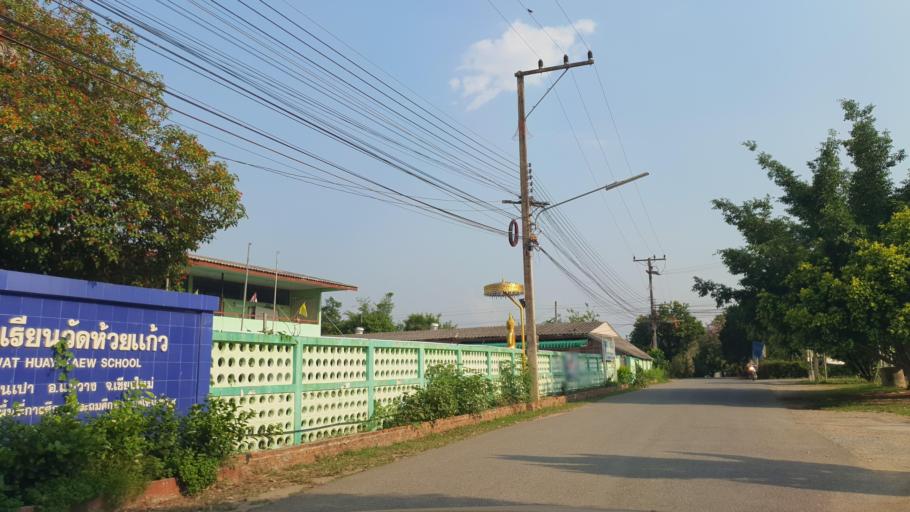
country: TH
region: Chiang Mai
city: Mae Wang
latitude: 18.6724
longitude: 98.8140
